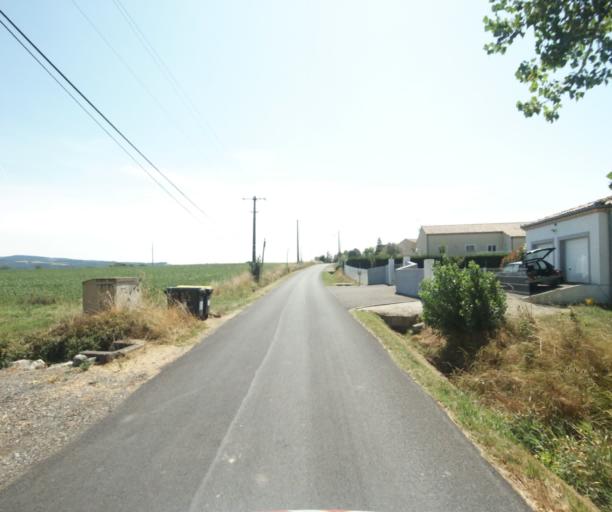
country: FR
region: Midi-Pyrenees
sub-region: Departement de la Haute-Garonne
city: Revel
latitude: 43.4843
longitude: 2.0126
